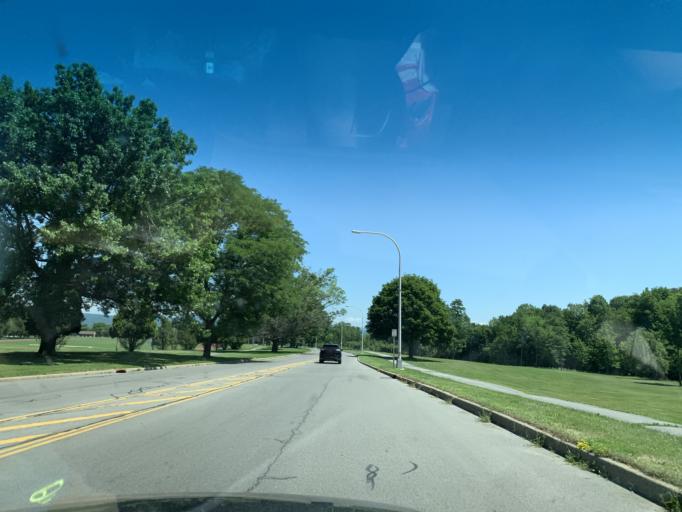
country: US
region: New York
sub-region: Oneida County
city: Utica
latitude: 43.0731
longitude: -75.2166
